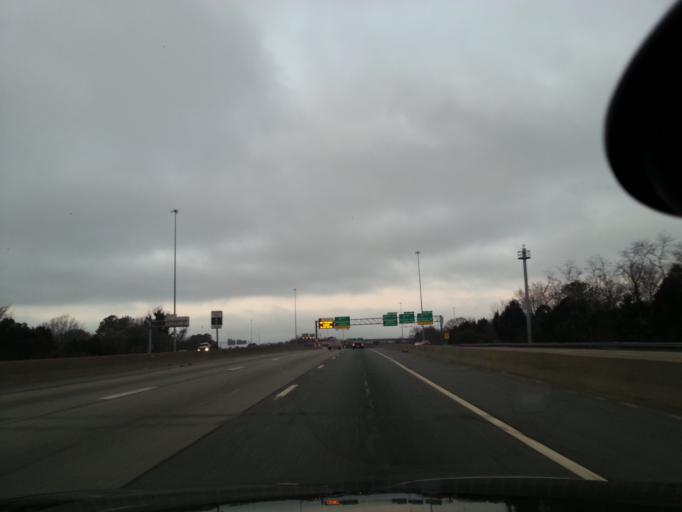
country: US
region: Virginia
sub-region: City of Chesapeake
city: Chesapeake
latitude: 36.8460
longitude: -76.1884
